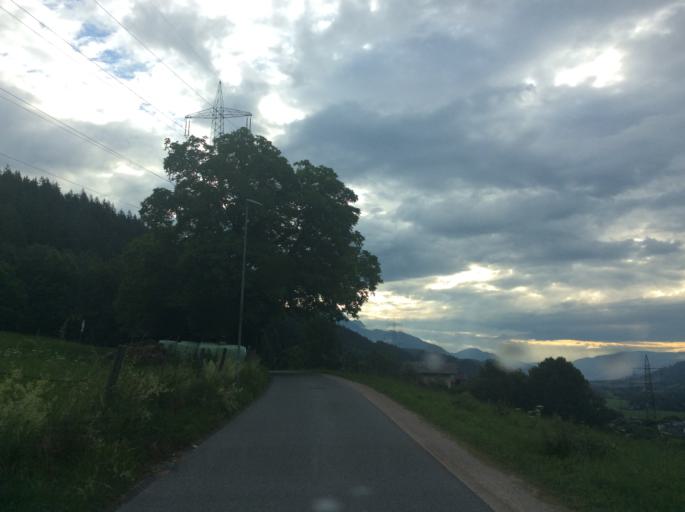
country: AT
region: Styria
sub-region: Politischer Bezirk Liezen
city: Schladming
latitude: 47.4027
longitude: 13.6984
